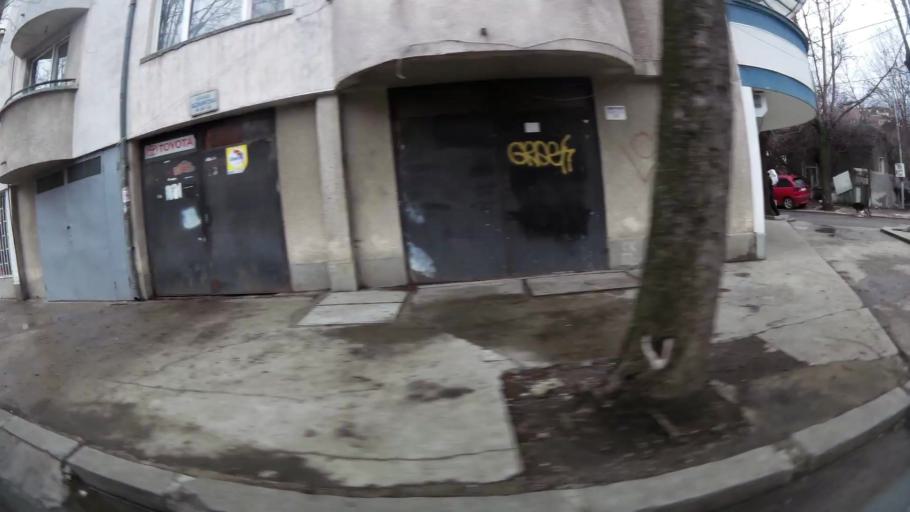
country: BG
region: Sofia-Capital
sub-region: Stolichna Obshtina
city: Sofia
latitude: 42.7214
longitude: 23.3066
